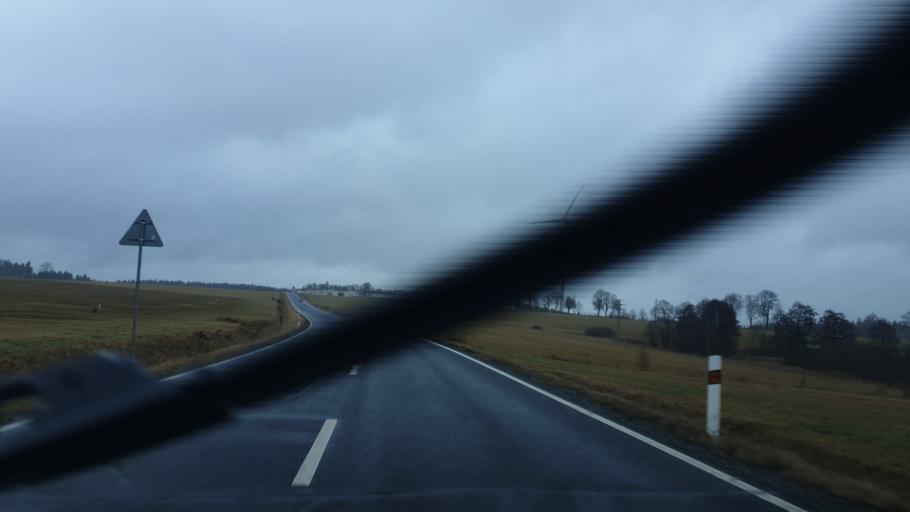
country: CZ
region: Karlovarsky
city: Hranice
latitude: 50.3108
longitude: 12.1664
